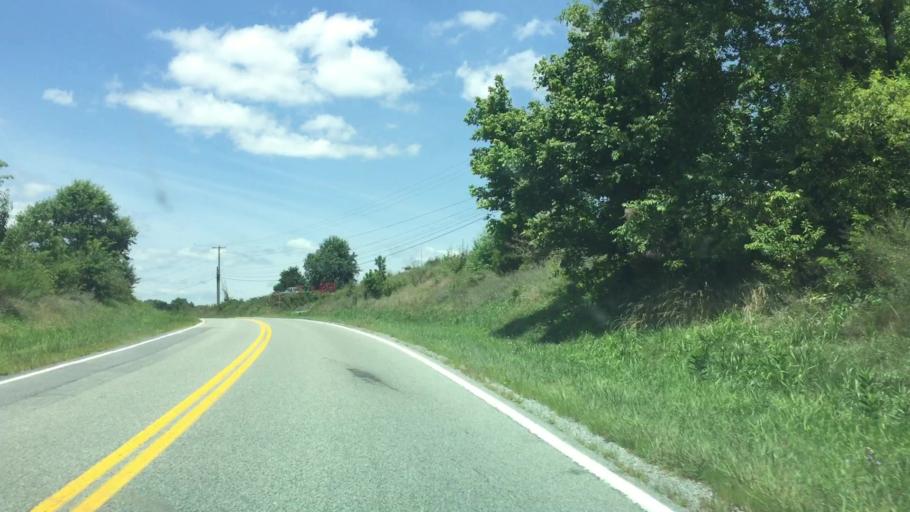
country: US
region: Virginia
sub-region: Wythe County
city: Wytheville
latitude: 36.9506
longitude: -80.9223
